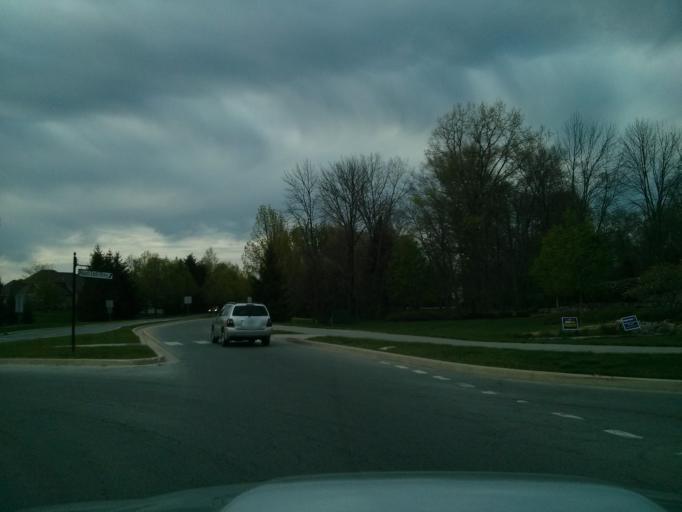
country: US
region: Indiana
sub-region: Hamilton County
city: Carmel
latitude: 39.9922
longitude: -86.0703
